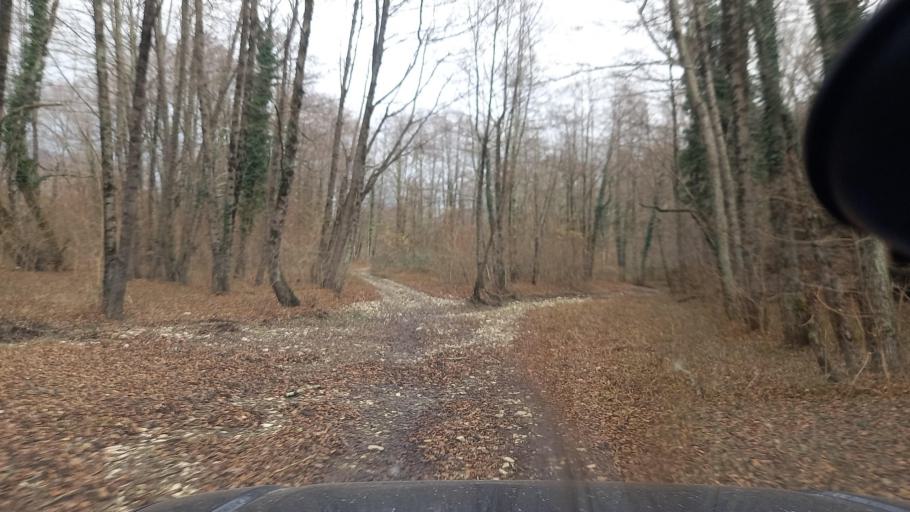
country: RU
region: Krasnodarskiy
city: Pshada
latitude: 44.4869
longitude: 38.4125
